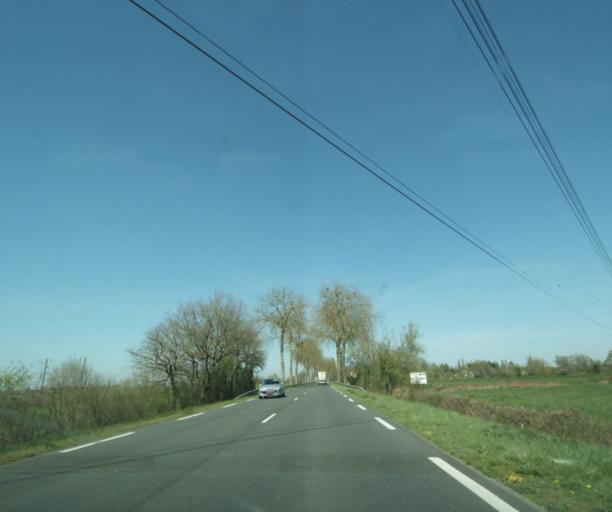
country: FR
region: Bourgogne
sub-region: Departement de la Nievre
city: Chantenay-Saint-Imbert
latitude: 46.6925
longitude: 3.2138
